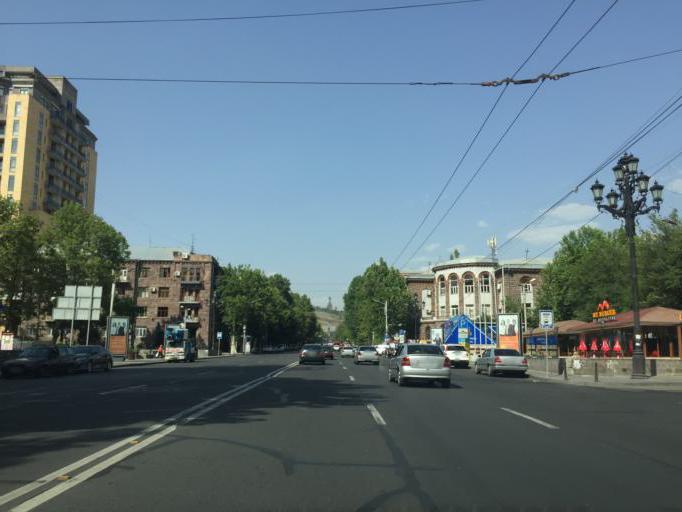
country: AM
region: Yerevan
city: Yerevan
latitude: 40.1817
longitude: 44.5087
